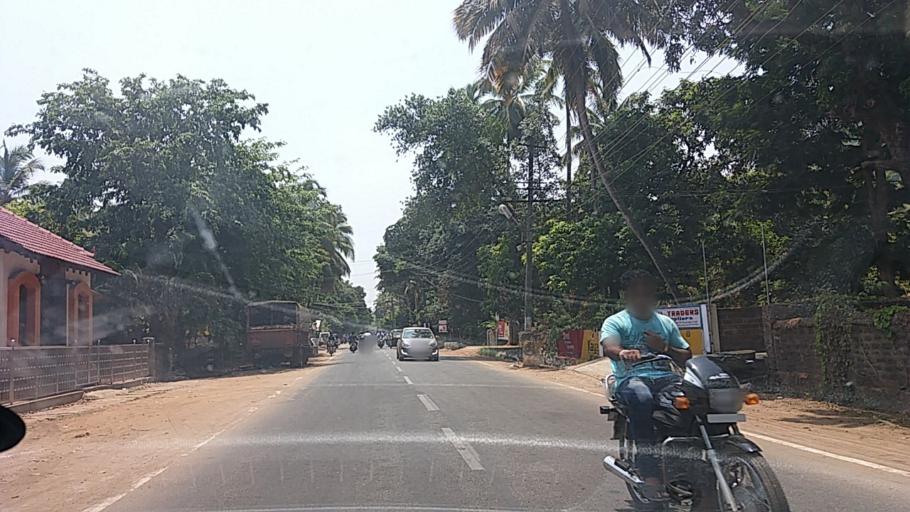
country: IN
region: Karnataka
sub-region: Uttar Kannada
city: Karwar
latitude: 14.8094
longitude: 74.1358
